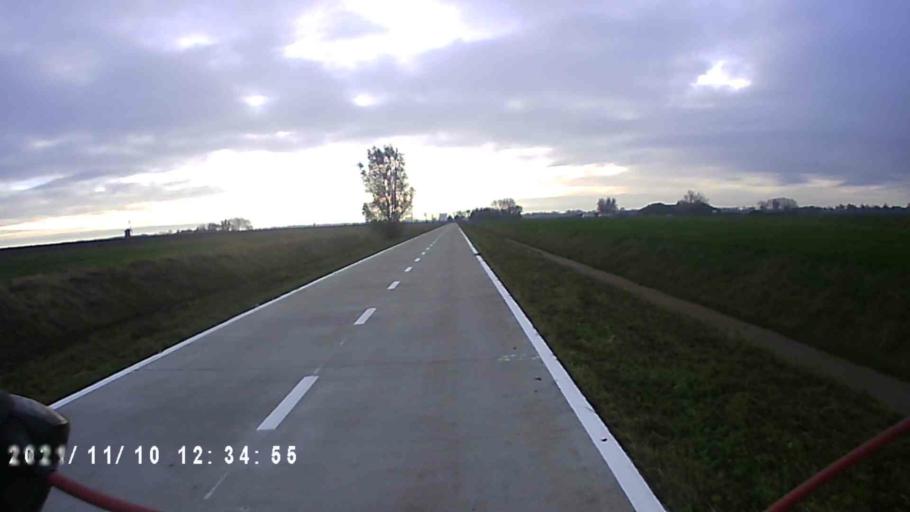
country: NL
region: Groningen
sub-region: Gemeente Groningen
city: Korrewegwijk
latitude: 53.2682
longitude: 6.5440
